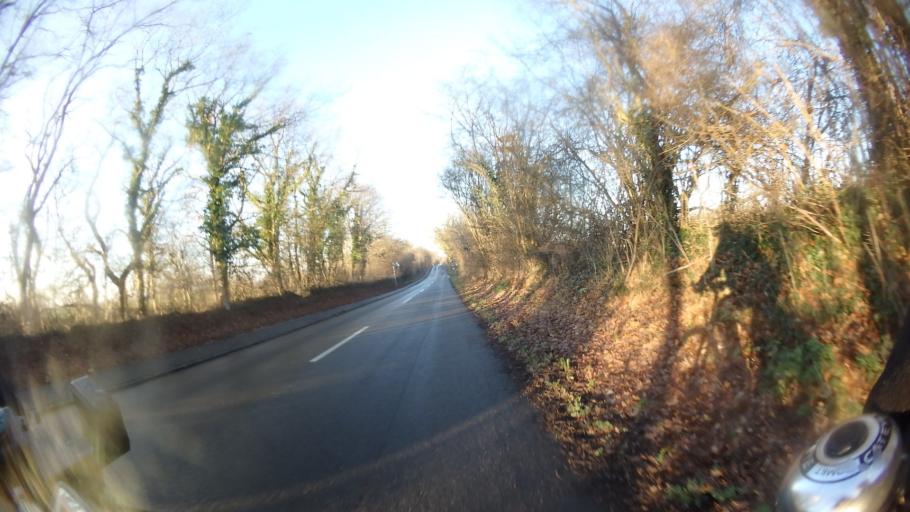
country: DE
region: Schleswig-Holstein
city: Travemuende
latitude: 53.9749
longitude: 10.8671
